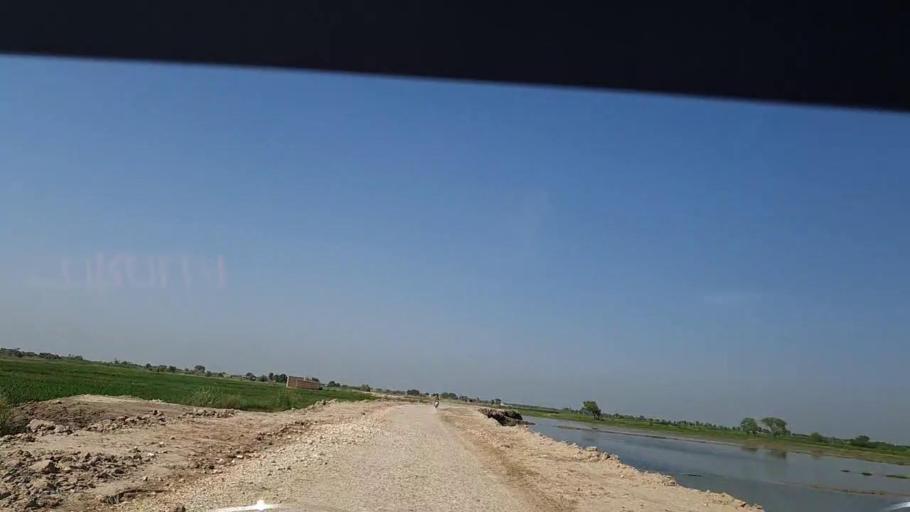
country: PK
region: Sindh
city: Tangwani
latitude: 28.3176
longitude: 69.0829
